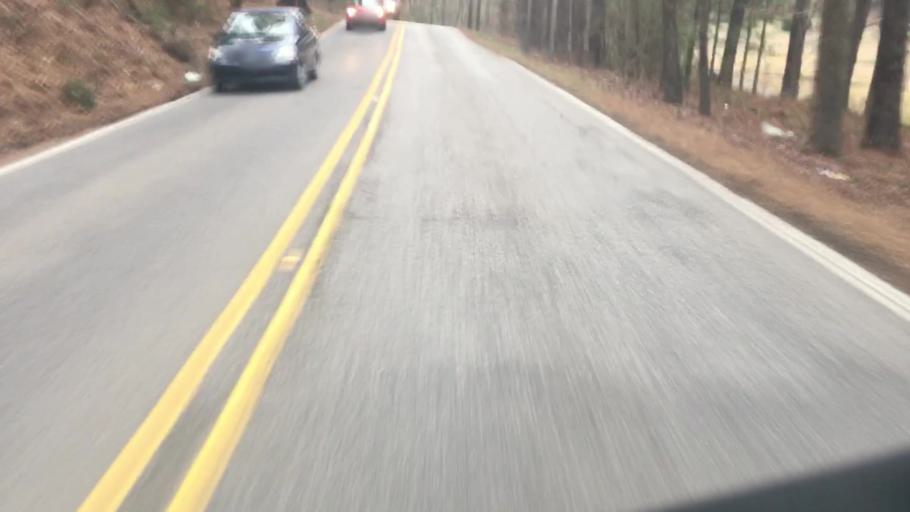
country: US
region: Alabama
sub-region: Jefferson County
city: Vestavia Hills
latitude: 33.4170
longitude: -86.7516
